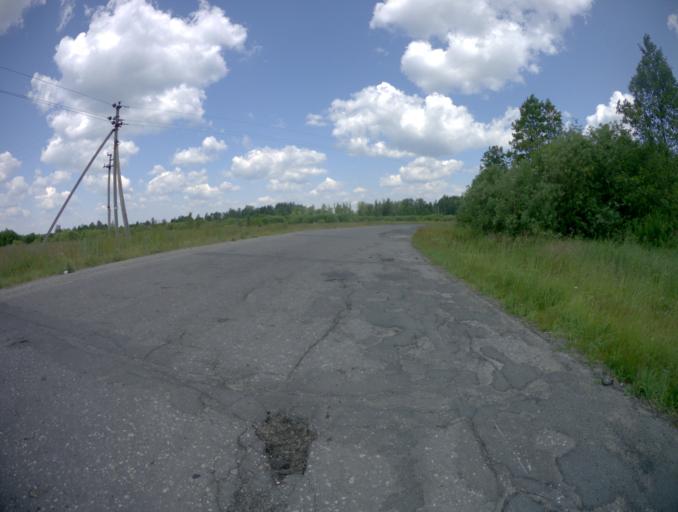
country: RU
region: Vladimir
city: Vyazniki
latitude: 56.3239
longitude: 42.1198
